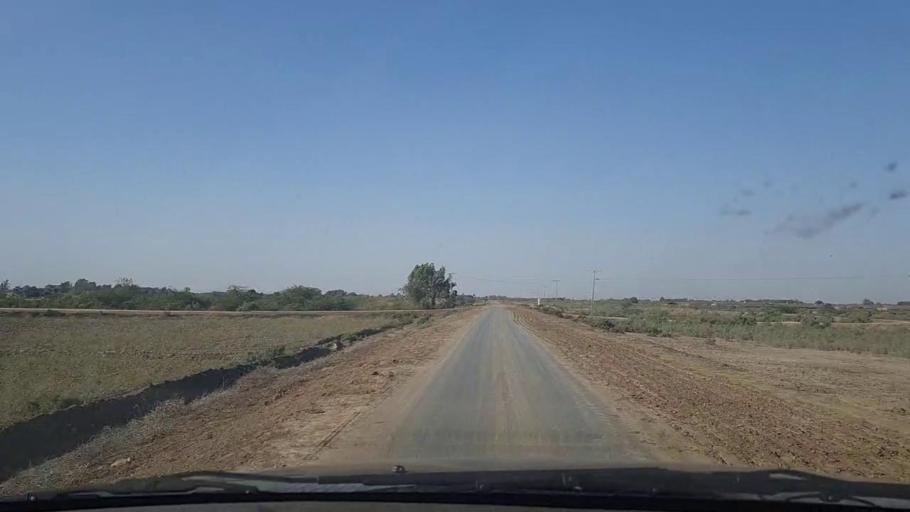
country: PK
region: Sindh
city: Chuhar Jamali
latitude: 24.3152
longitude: 67.7547
